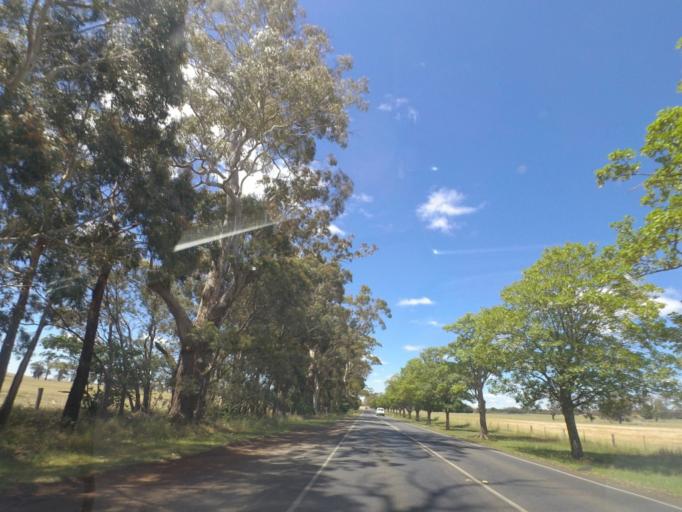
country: AU
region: Victoria
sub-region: Mount Alexander
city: Castlemaine
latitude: -37.3343
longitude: 144.1701
